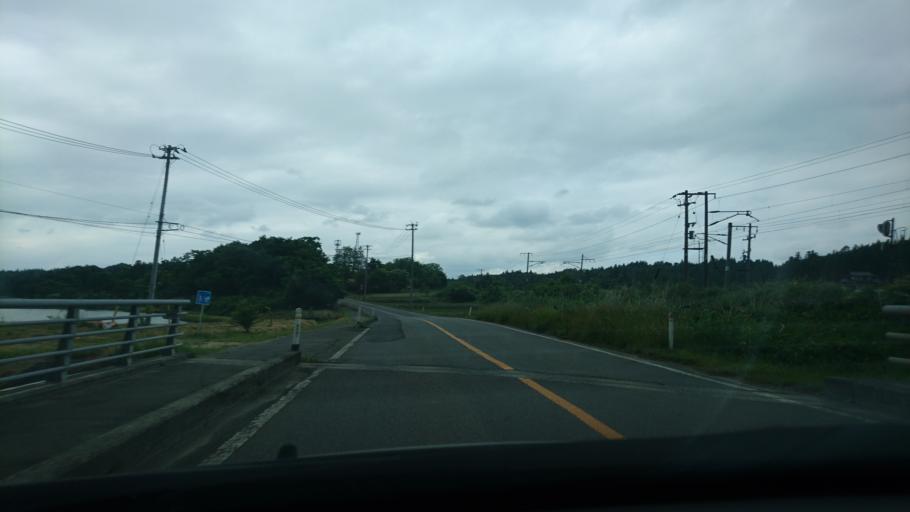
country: JP
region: Iwate
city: Ichinoseki
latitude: 38.8166
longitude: 141.1815
